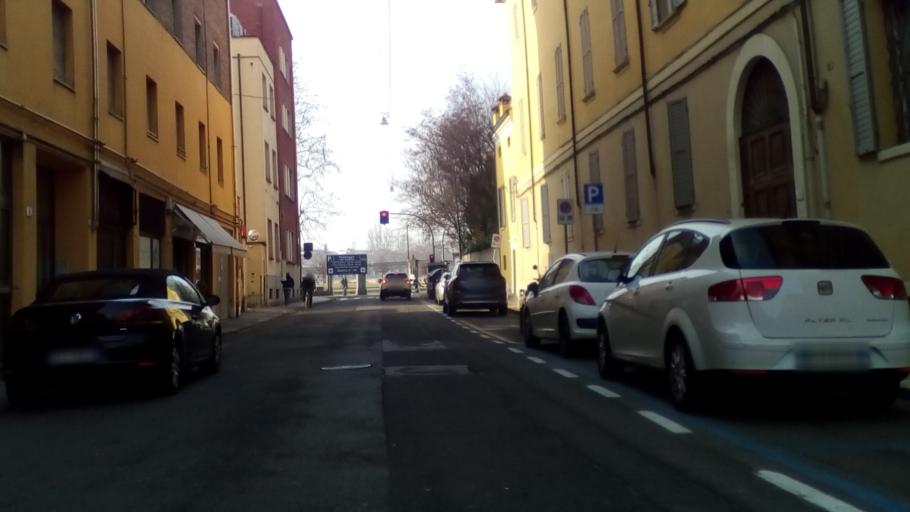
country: IT
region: Emilia-Romagna
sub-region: Provincia di Modena
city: Modena
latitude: 44.6507
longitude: 10.9263
